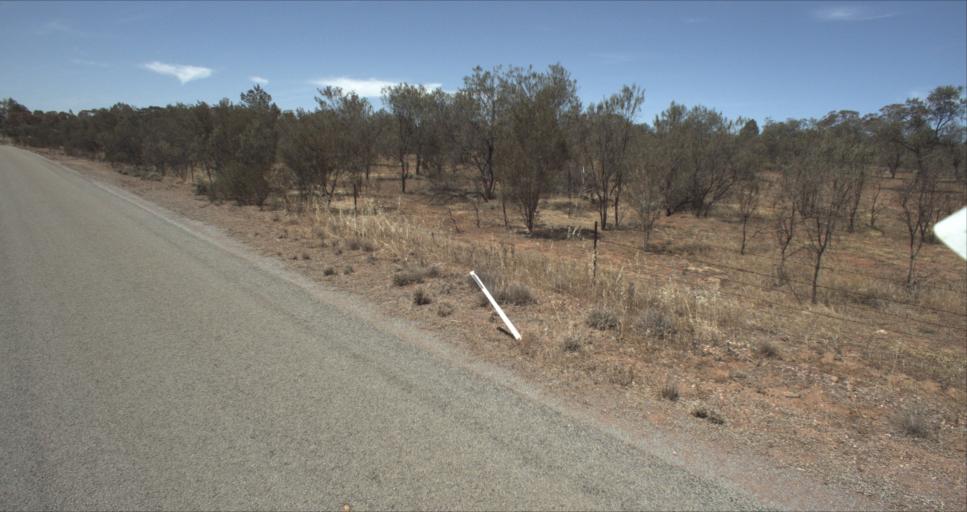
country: AU
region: New South Wales
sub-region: Leeton
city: Leeton
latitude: -34.5814
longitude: 146.4307
